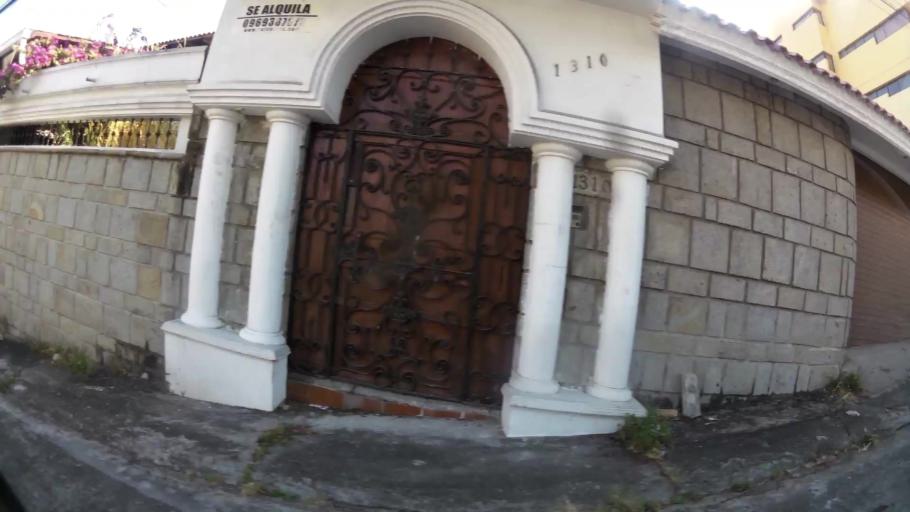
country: EC
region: Guayas
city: Guayaquil
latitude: -2.1634
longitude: -79.9062
